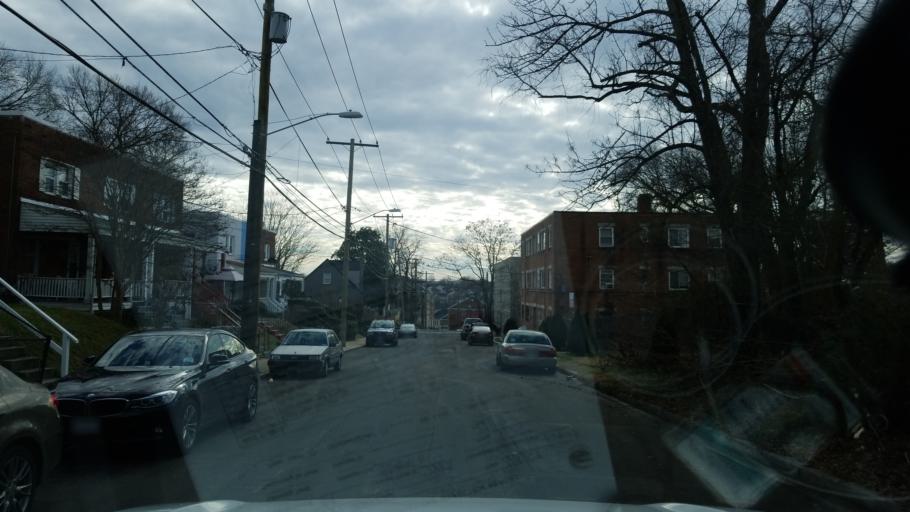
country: US
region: Maryland
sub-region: Prince George's County
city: Glassmanor
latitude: 38.8420
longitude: -76.9921
